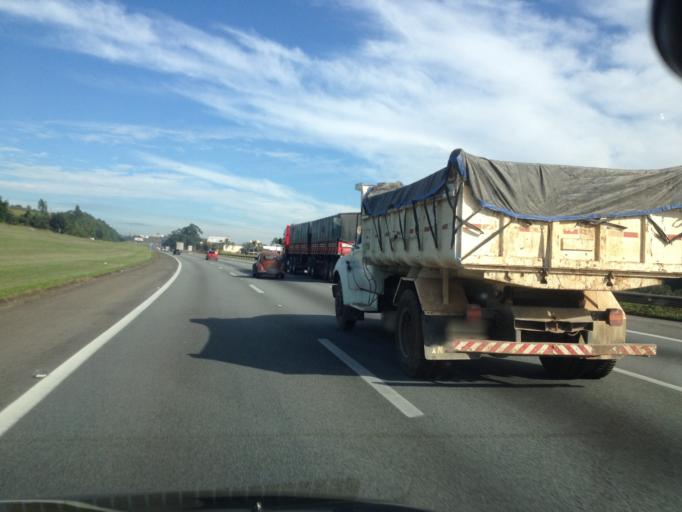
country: BR
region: Sao Paulo
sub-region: Mairinque
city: Mairinque
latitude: -23.4185
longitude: -47.2192
